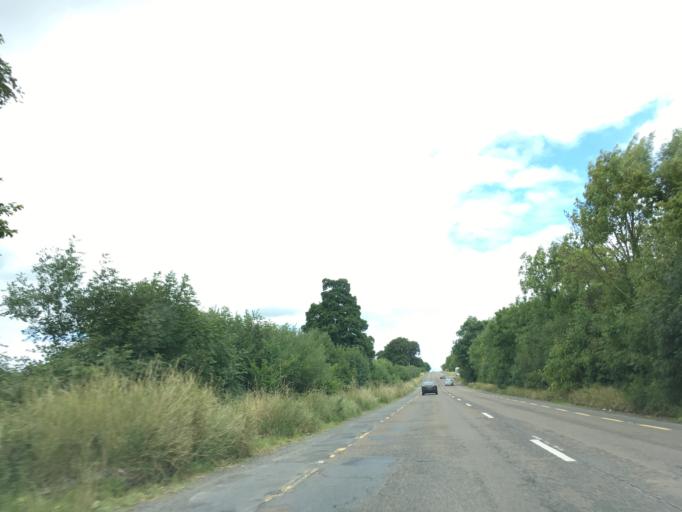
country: IE
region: Munster
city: Cashel
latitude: 52.4855
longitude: -7.8913
